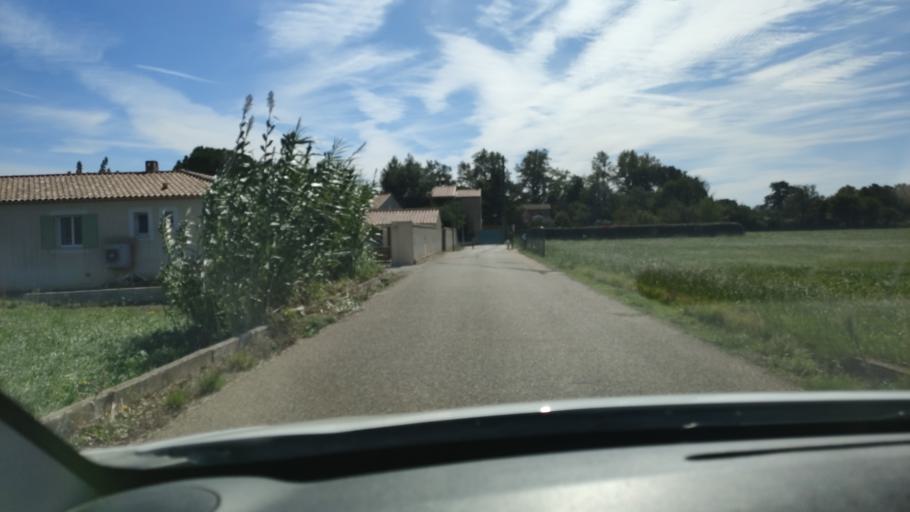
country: FR
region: Provence-Alpes-Cote d'Azur
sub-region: Departement du Vaucluse
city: Morieres-les-Avignon
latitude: 43.9484
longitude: 4.8866
